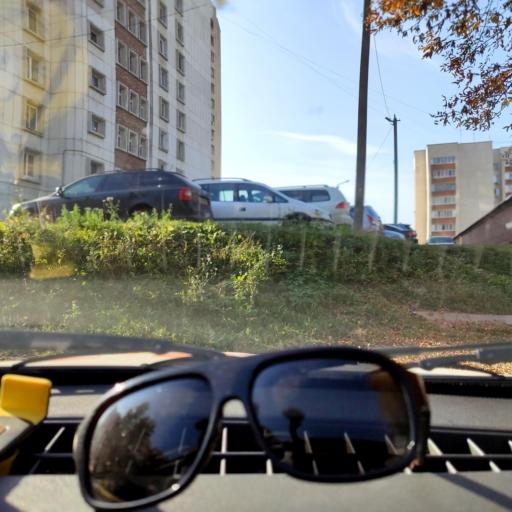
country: RU
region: Bashkortostan
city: Ufa
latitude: 54.7121
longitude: 55.9766
